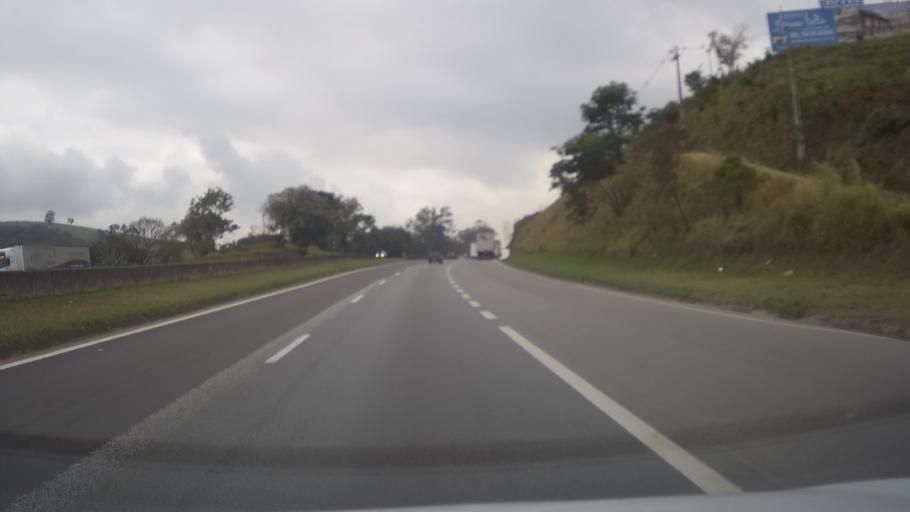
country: BR
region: Minas Gerais
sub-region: Extrema
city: Extrema
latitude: -22.8773
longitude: -46.3701
